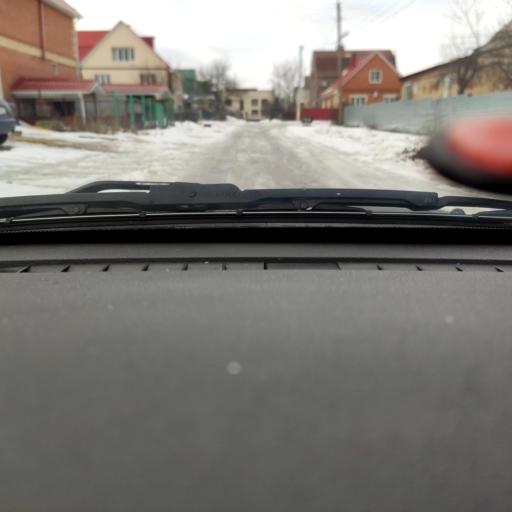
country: RU
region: Voronezj
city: Semiluki
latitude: 51.7111
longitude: 39.0305
